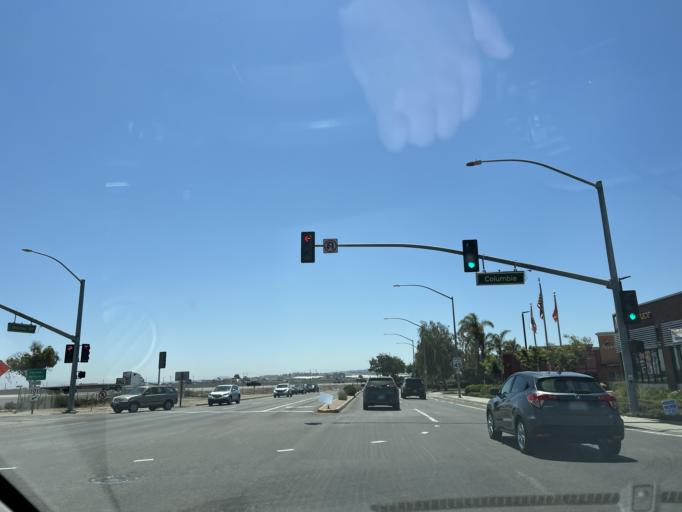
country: US
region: California
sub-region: Santa Barbara County
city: Santa Maria
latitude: 34.9361
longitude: -120.4189
